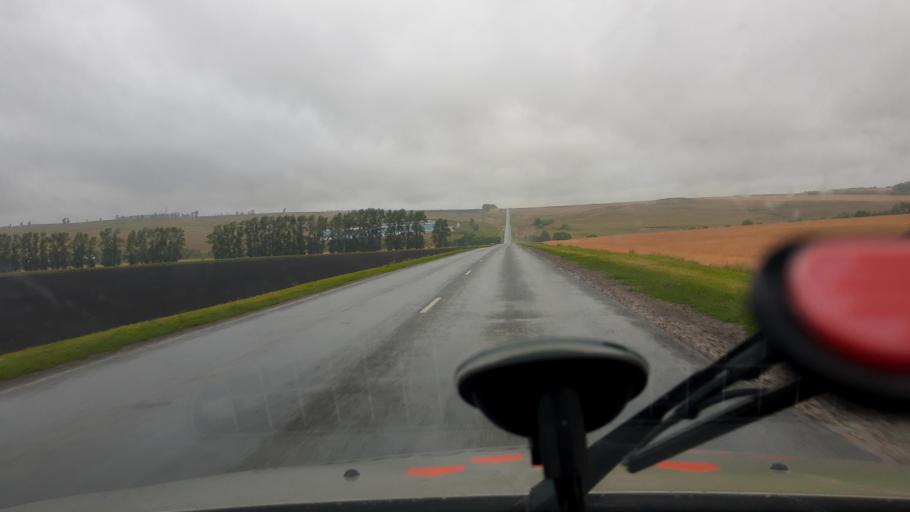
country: RU
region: Bashkortostan
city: Chekmagush
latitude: 55.0559
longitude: 54.6232
